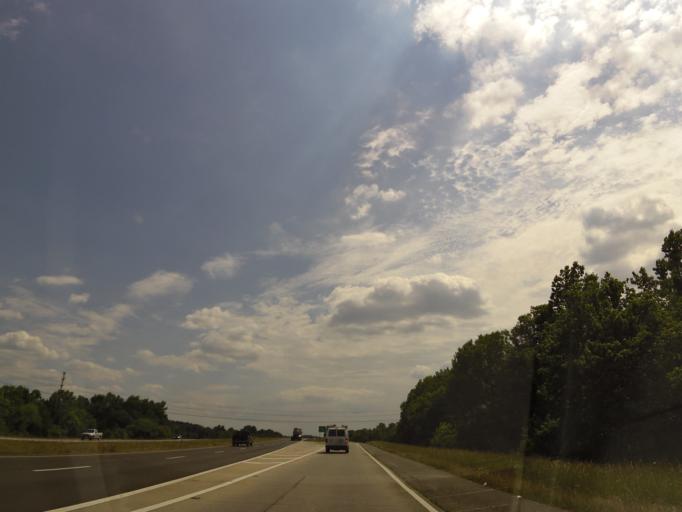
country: US
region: Tennessee
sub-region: Marion County
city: Jasper
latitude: 35.0761
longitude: -85.6124
